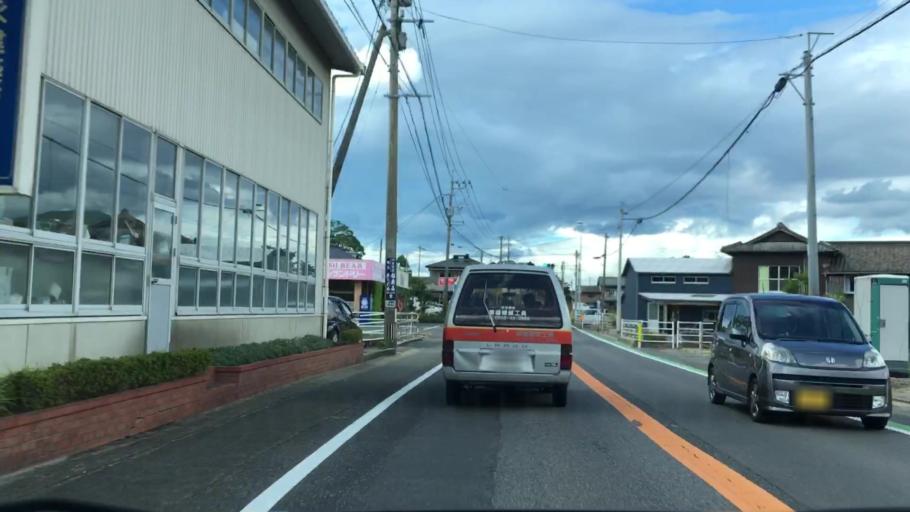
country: JP
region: Saga Prefecture
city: Imaricho-ko
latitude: 33.2031
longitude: 129.8502
